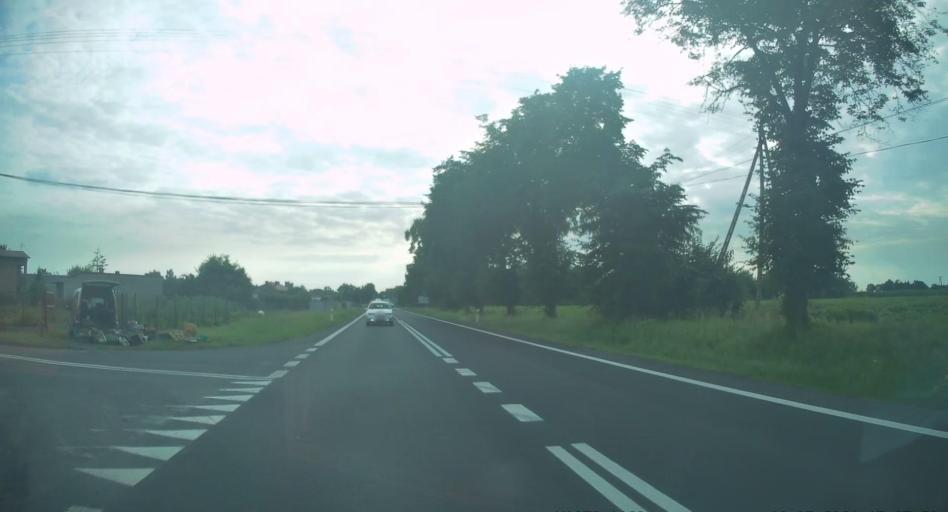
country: PL
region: Silesian Voivodeship
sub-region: Powiat czestochowski
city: Klomnice
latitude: 50.9131
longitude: 19.3141
